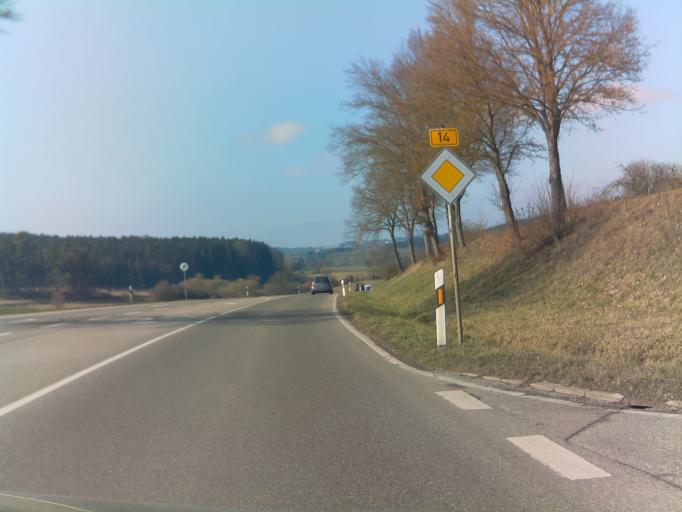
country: DE
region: Baden-Wuerttemberg
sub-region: Karlsruhe Region
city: Horb am Neckar
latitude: 48.4760
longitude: 8.7360
